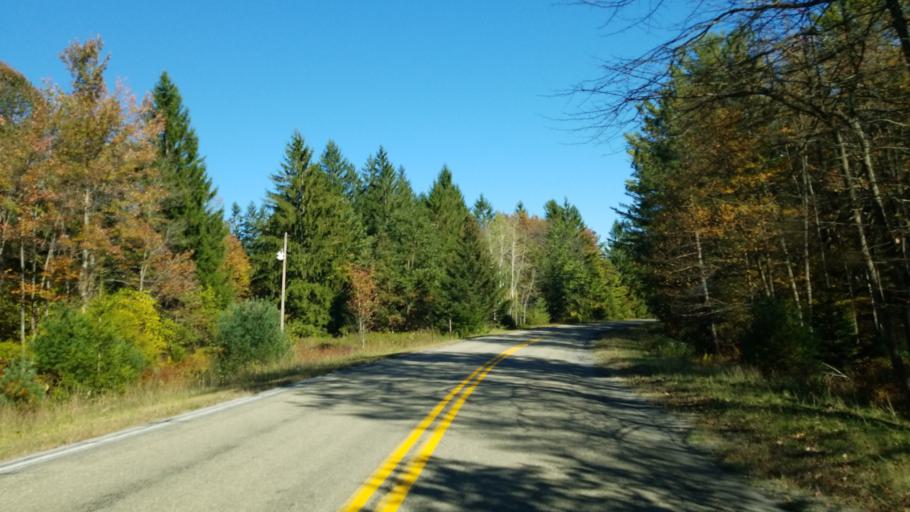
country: US
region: Pennsylvania
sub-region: Clearfield County
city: Shiloh
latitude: 41.2618
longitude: -78.2981
